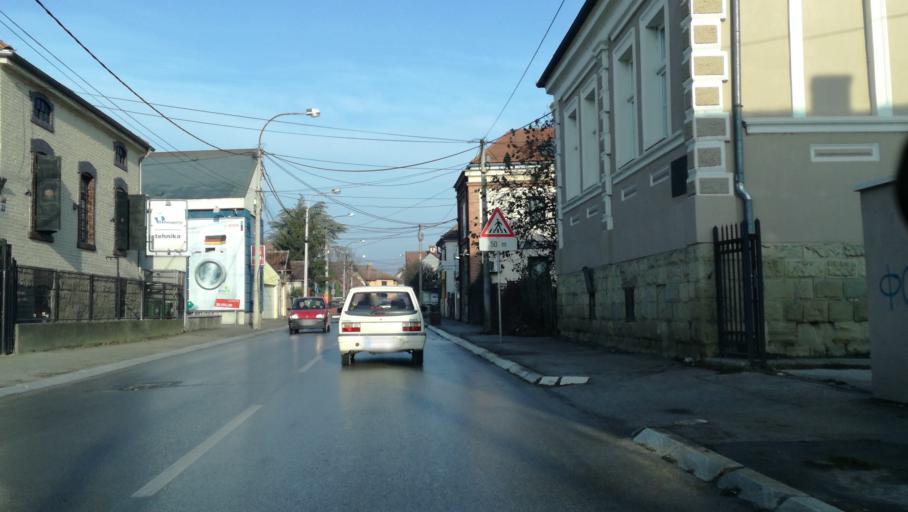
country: RS
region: Central Serbia
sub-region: Moravicki Okrug
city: Cacak
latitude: 43.8916
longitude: 20.3531
